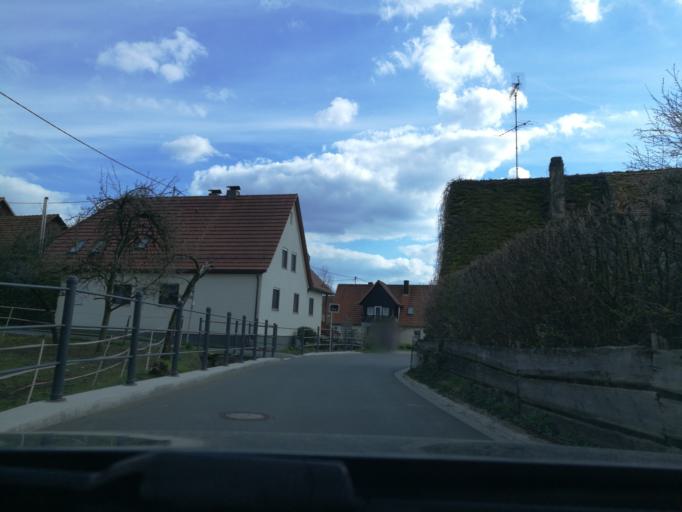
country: DE
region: Bavaria
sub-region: Upper Franconia
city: Weilersbach
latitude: 49.8197
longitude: 11.1160
